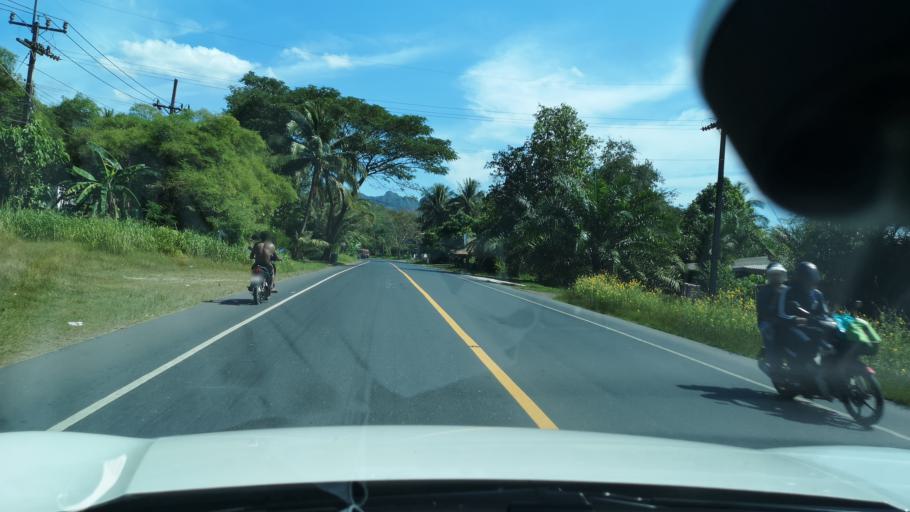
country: TH
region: Phangnga
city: Phang Nga
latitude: 8.5352
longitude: 98.5012
